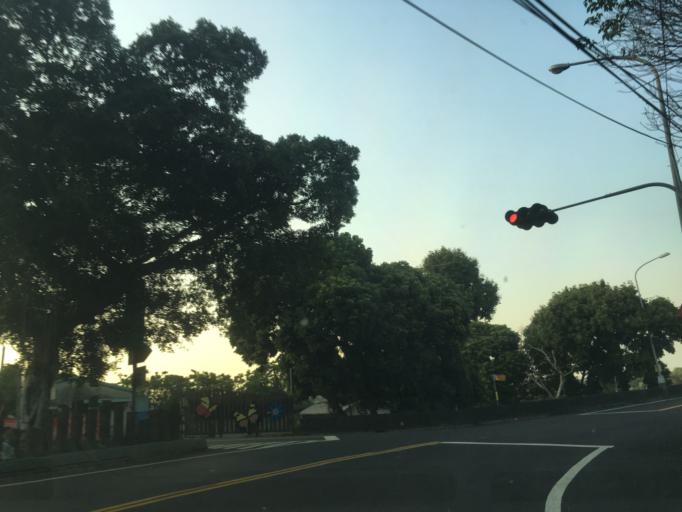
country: TW
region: Taiwan
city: Zhongxing New Village
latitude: 23.9515
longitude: 120.6568
